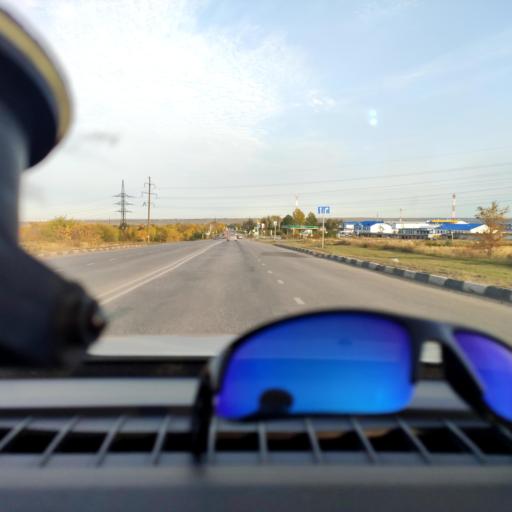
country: RU
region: Samara
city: Novokuybyshevsk
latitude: 53.0775
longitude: 49.9657
